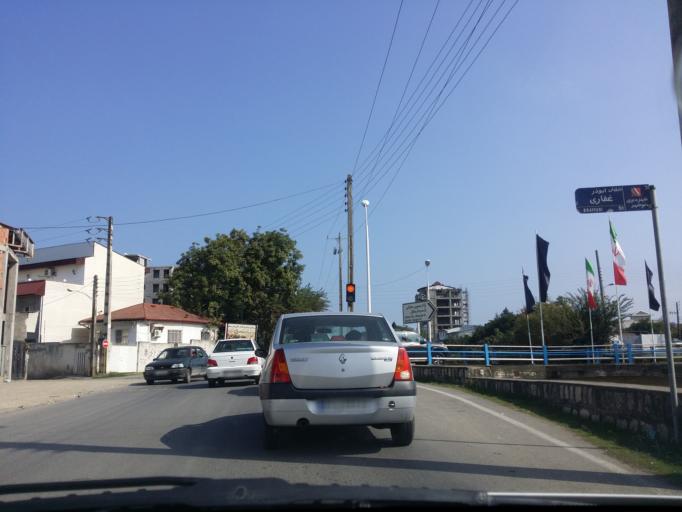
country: IR
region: Mazandaran
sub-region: Nowshahr
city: Nowshahr
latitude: 36.6456
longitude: 51.5039
